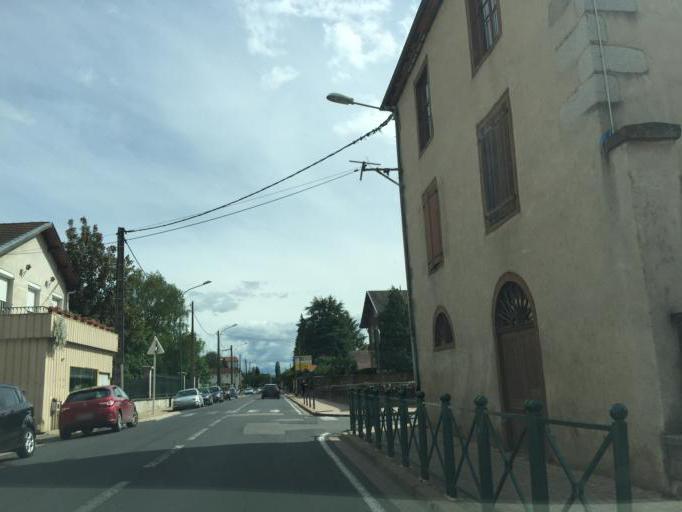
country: FR
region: Auvergne
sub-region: Departement du Puy-de-Dome
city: Ambert
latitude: 45.5467
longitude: 3.7389
